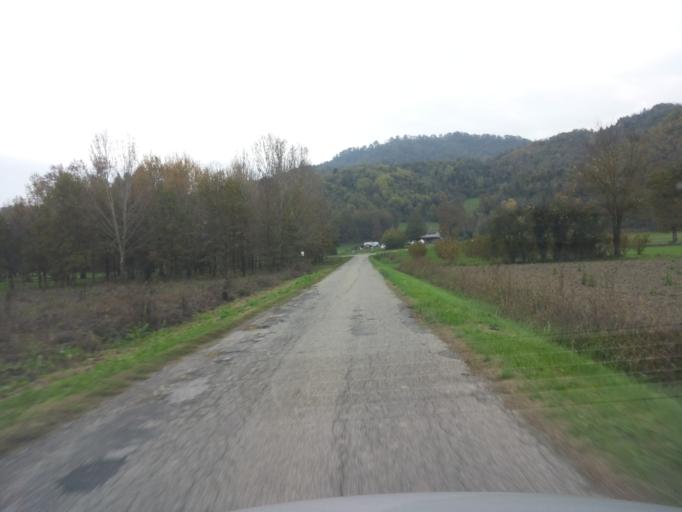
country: IT
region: Piedmont
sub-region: Provincia di Alessandria
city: Serralunga di Crea
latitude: 45.1095
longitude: 8.2733
